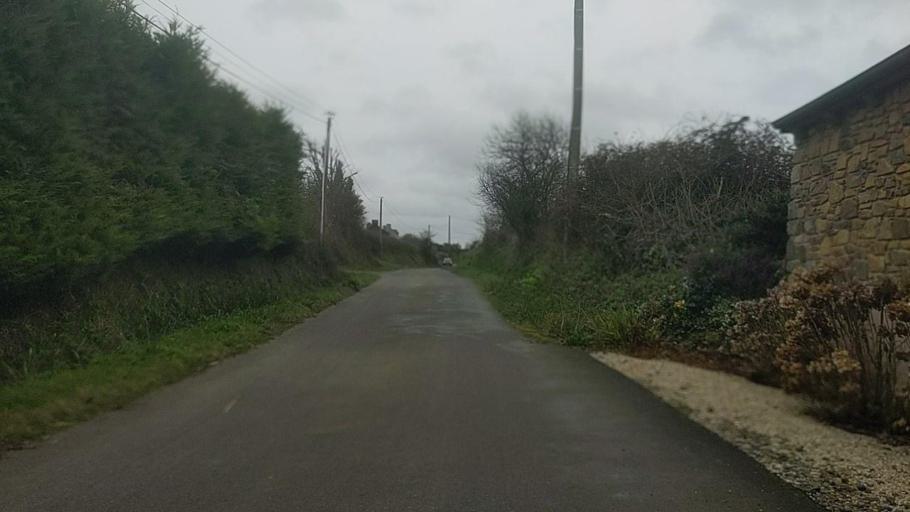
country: FR
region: Brittany
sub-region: Departement des Cotes-d'Armor
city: Pleumeur-Gautier
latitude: 48.8266
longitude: -3.1798
